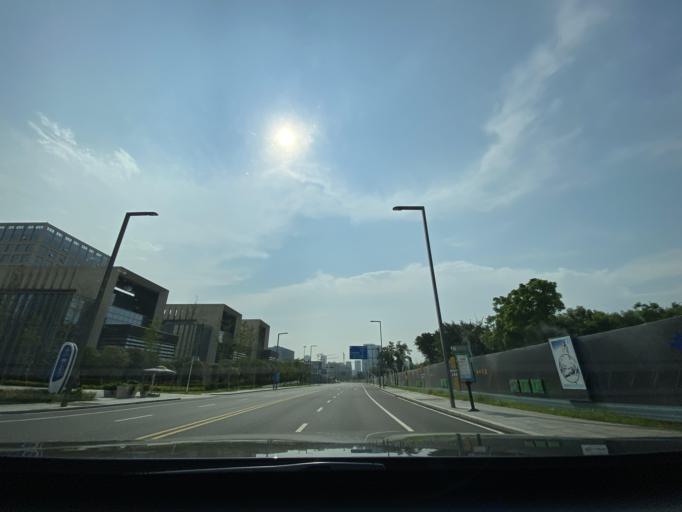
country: CN
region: Sichuan
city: Dongsheng
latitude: 30.3927
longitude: 104.0838
